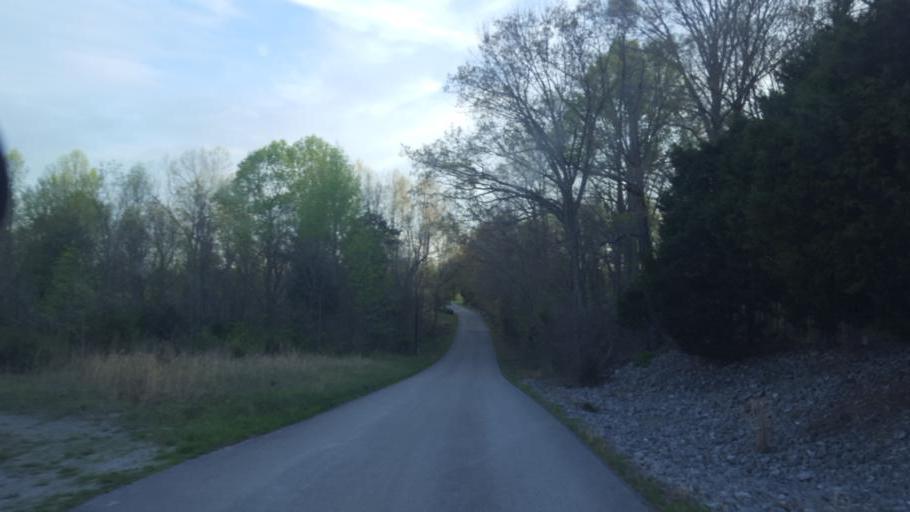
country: US
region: Kentucky
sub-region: Barren County
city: Cave City
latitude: 37.1459
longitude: -86.0222
